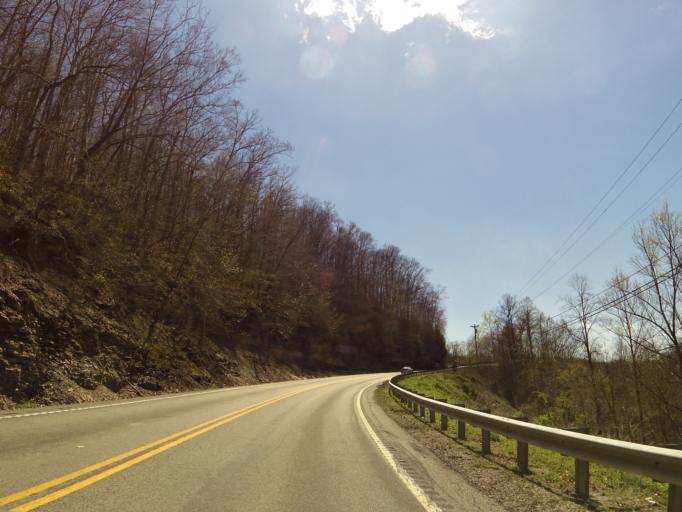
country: US
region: Tennessee
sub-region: DeKalb County
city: Smithville
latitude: 35.9638
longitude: -85.7202
